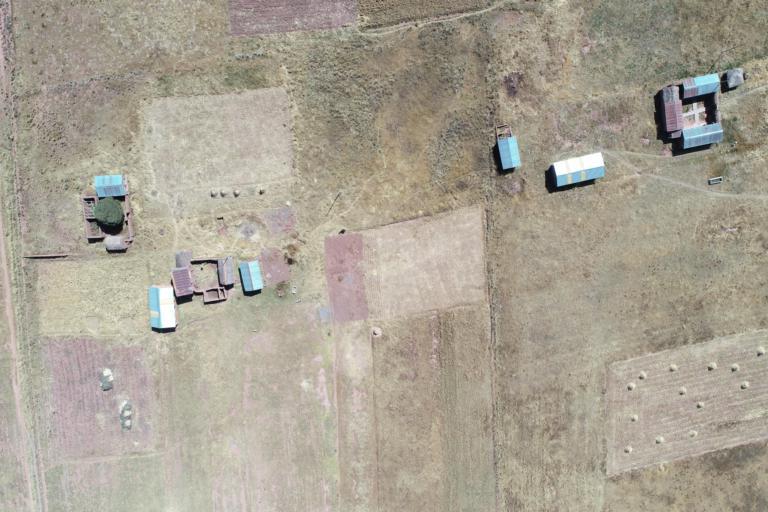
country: BO
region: La Paz
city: Tiahuanaco
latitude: -16.5916
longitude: -68.7538
